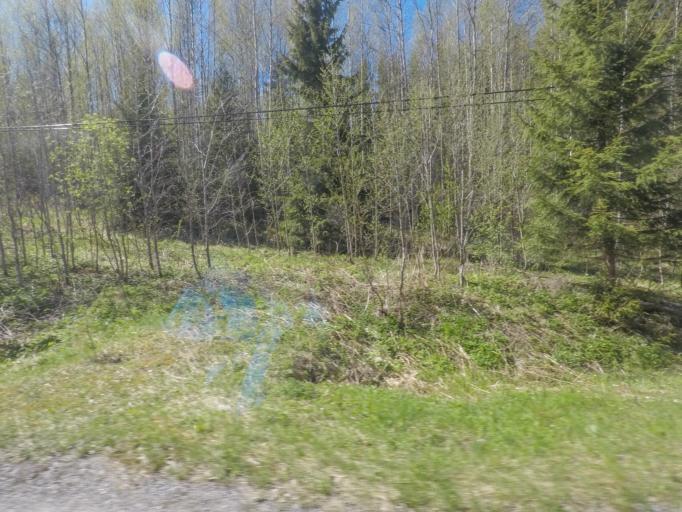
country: FI
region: Uusimaa
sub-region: Helsinki
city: Sammatti
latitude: 60.3724
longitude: 23.8117
